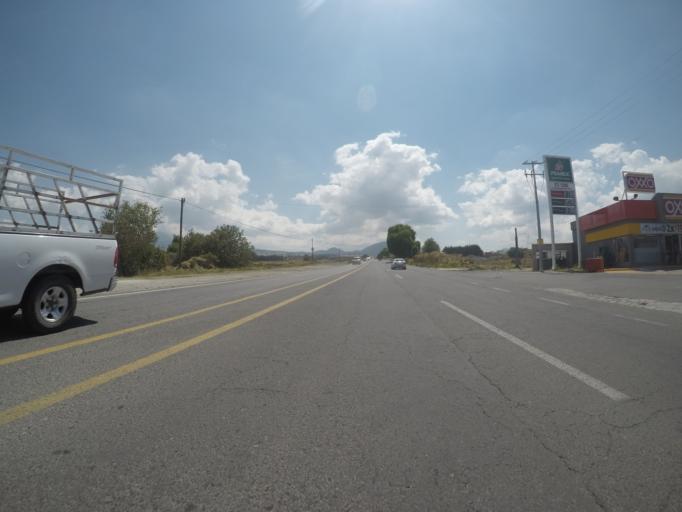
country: MX
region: Mexico
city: San Juan de las Huertas
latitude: 19.2406
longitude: -99.7712
